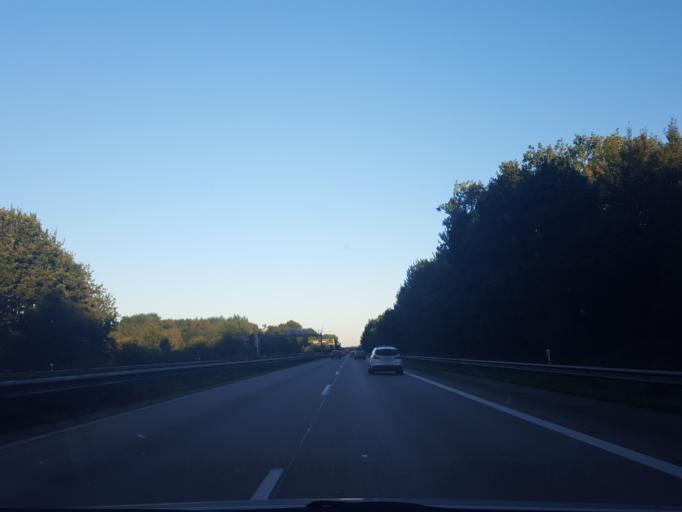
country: DE
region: Bremen
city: Bremen
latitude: 53.1158
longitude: 8.8358
